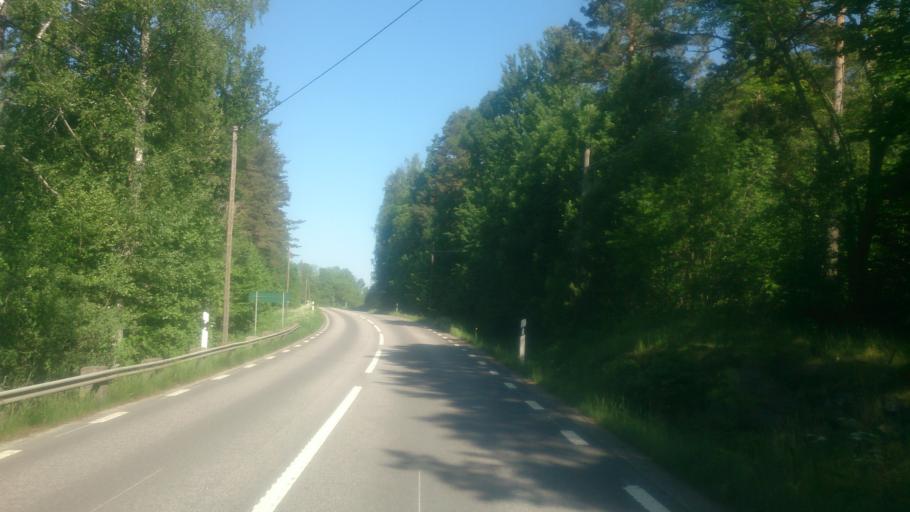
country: SE
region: OEstergoetland
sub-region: Atvidabergs Kommun
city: Atvidaberg
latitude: 58.1028
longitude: 16.1168
